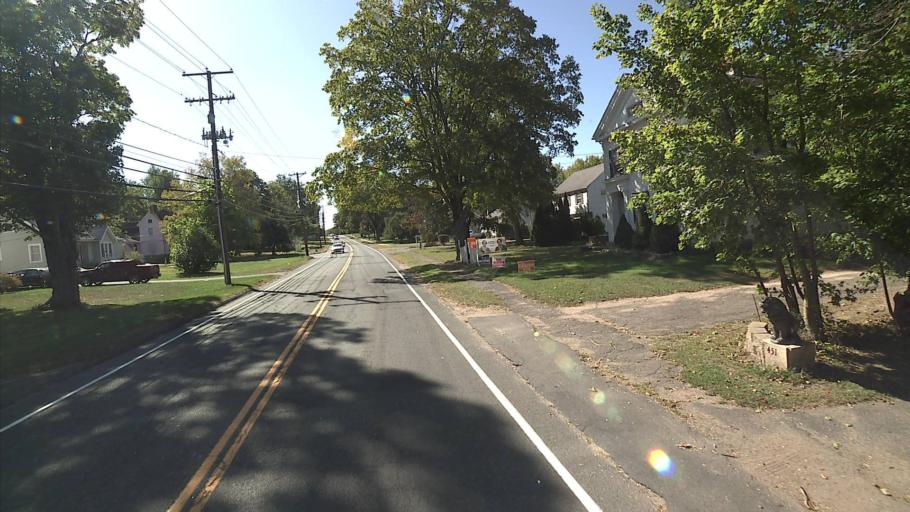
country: US
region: Connecticut
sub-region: Hartford County
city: Bristol
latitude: 41.6946
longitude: -72.9447
